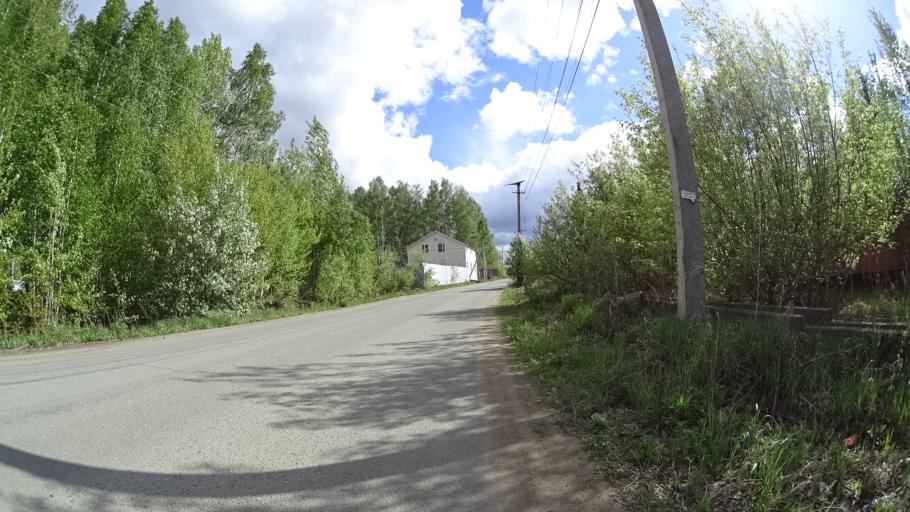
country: RU
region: Chelyabinsk
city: Sargazy
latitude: 55.1511
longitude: 61.2382
